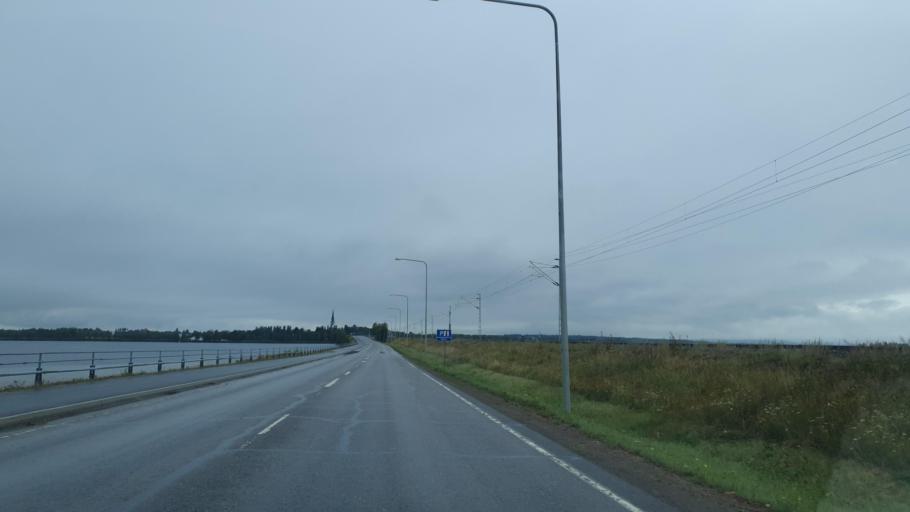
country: FI
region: Lapland
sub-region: Itae-Lappi
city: Kemijaervi
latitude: 66.7159
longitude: 27.4661
